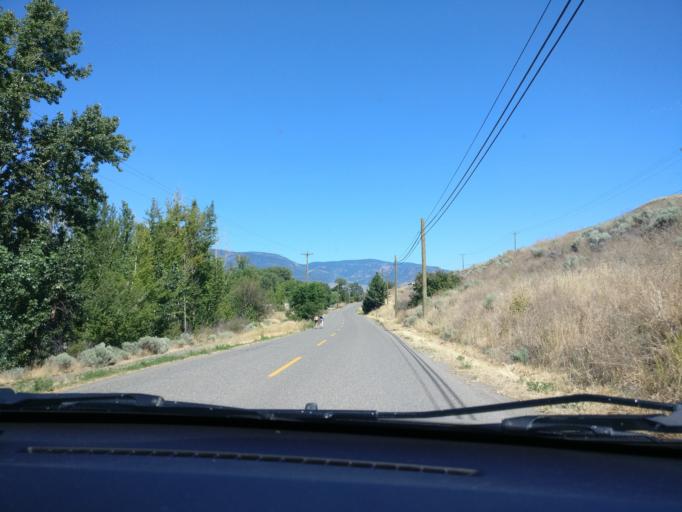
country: CA
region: British Columbia
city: Logan Lake
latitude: 50.7543
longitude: -120.8365
